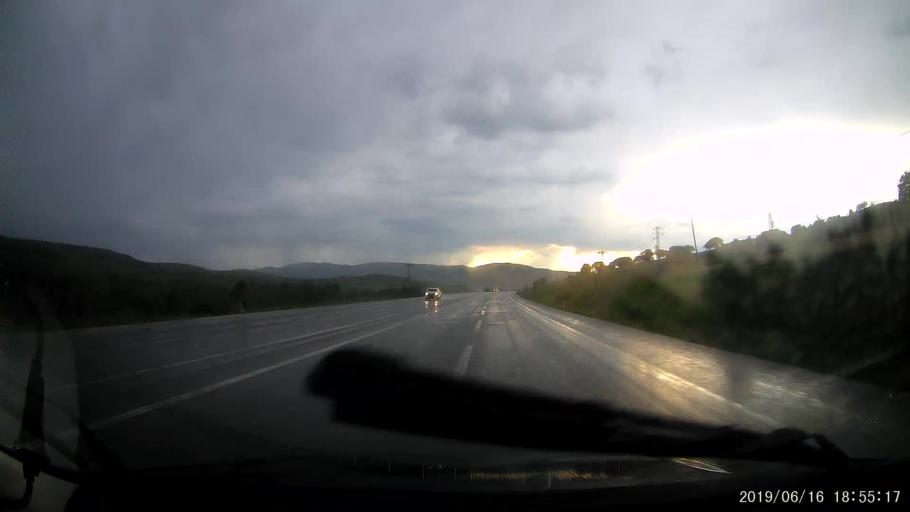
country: TR
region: Erzincan
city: Refahiye
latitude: 39.8994
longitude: 38.8317
